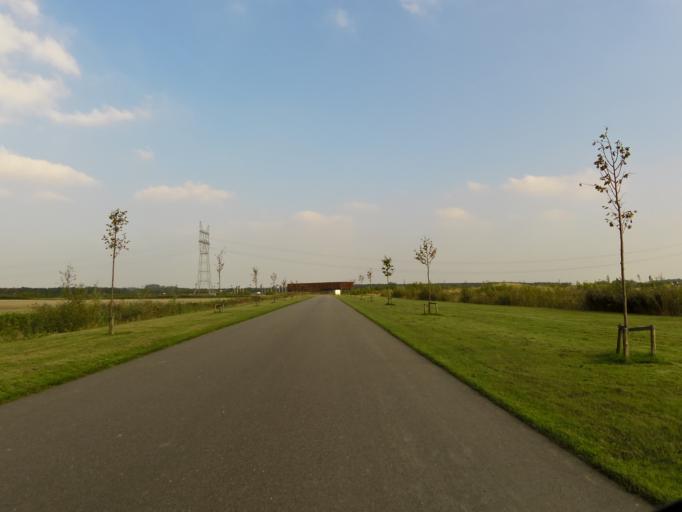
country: NL
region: South Holland
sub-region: Gemeente Rijnwoude
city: Benthuizen
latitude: 52.0734
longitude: 4.5663
